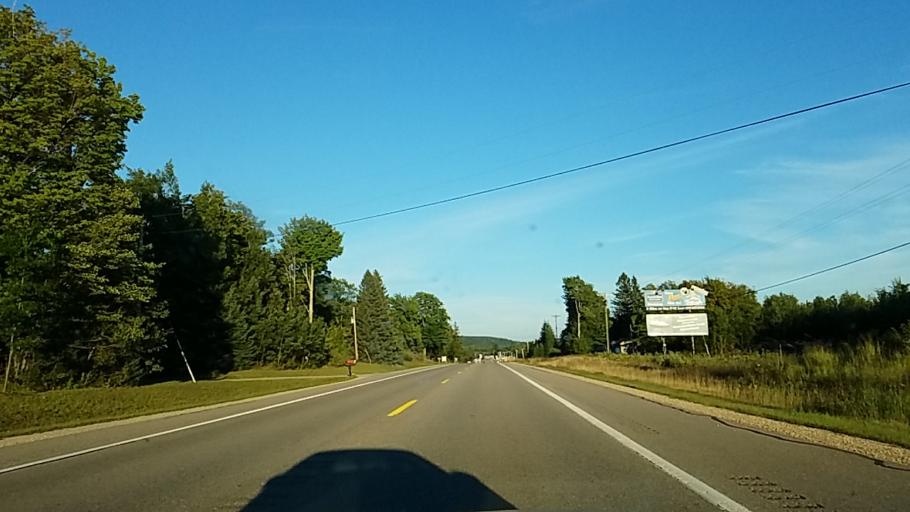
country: US
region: Michigan
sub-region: Alger County
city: Munising
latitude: 46.4398
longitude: -86.7177
